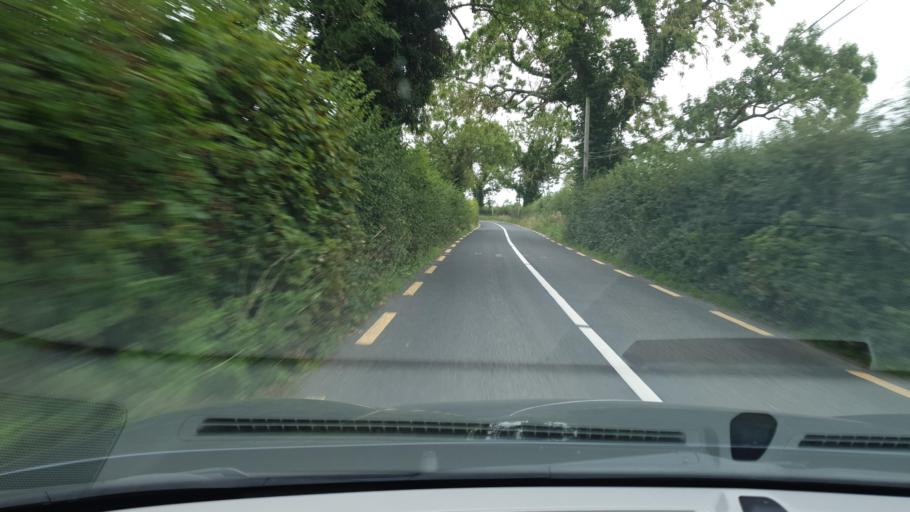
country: IE
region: Leinster
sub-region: Kildare
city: Kilcock
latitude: 53.4191
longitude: -6.6590
